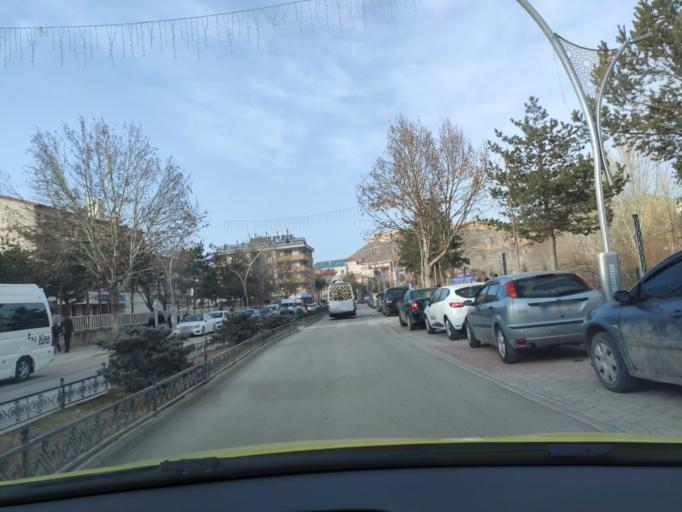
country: TR
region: Bayburt
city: Bayburt
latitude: 40.2557
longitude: 40.2257
